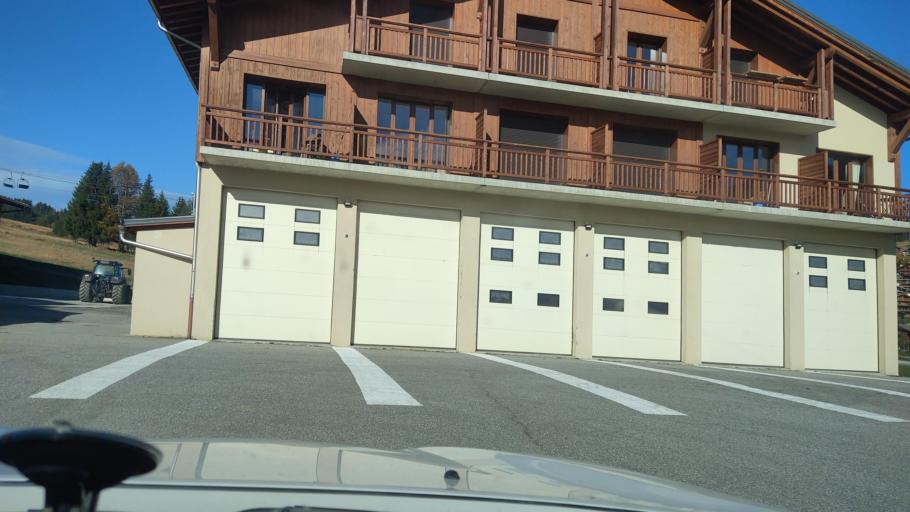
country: FR
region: Rhone-Alpes
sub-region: Departement de la Savoie
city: Beaufort
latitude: 45.7517
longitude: 6.5424
